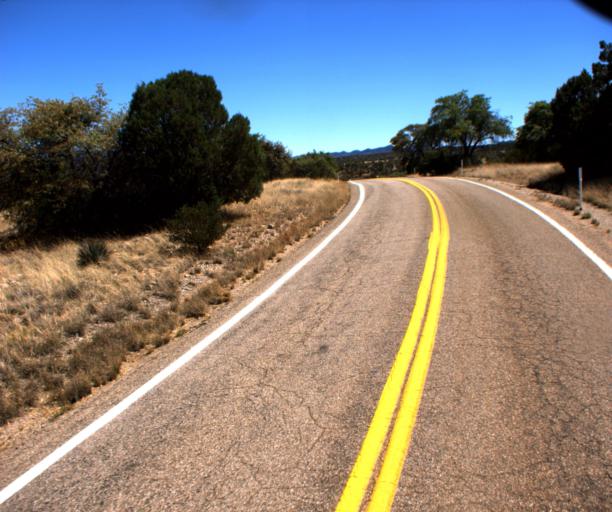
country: US
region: Arizona
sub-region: Cochise County
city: Huachuca City
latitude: 31.5675
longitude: -110.5598
